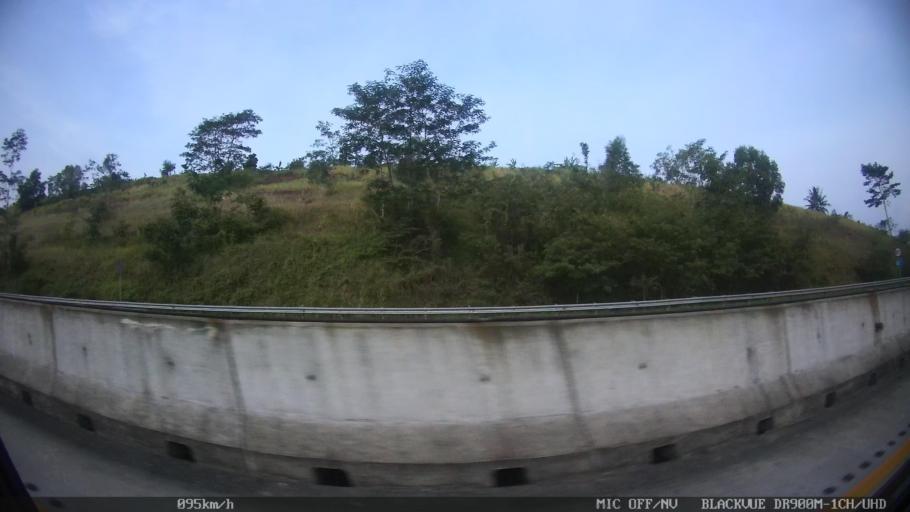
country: ID
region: Lampung
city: Penengahan
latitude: -5.8147
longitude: 105.7364
